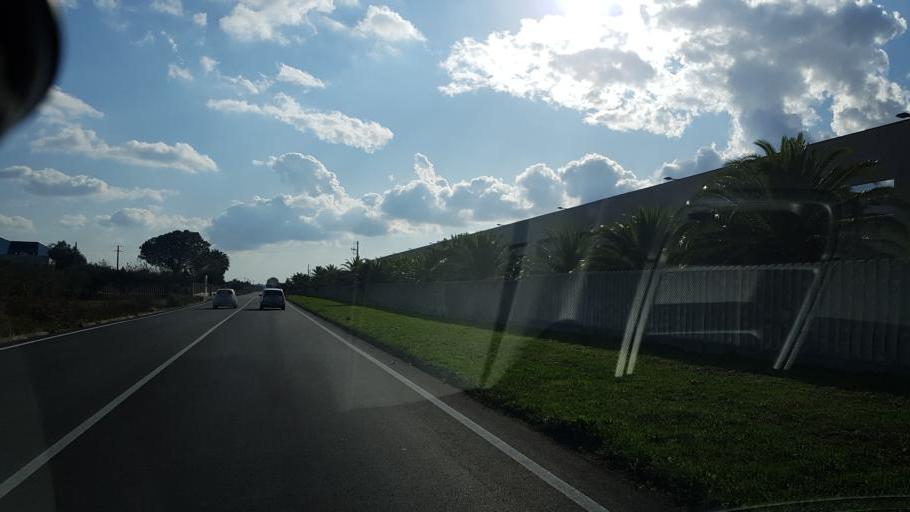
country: IT
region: Apulia
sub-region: Provincia di Lecce
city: Salice Salentino
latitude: 40.3677
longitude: 17.9672
